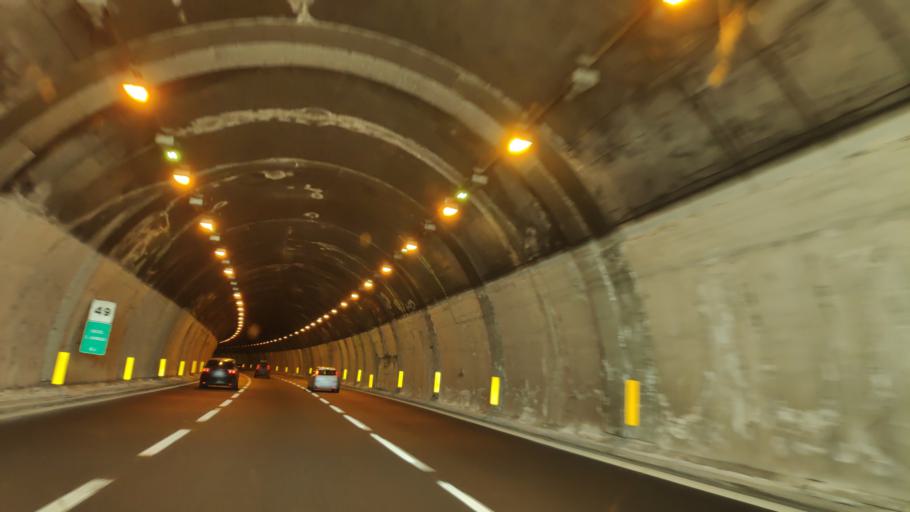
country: IT
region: Campania
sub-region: Provincia di Salerno
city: Piazza del Galdo-Sant'Angelo
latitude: 40.7727
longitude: 14.7189
